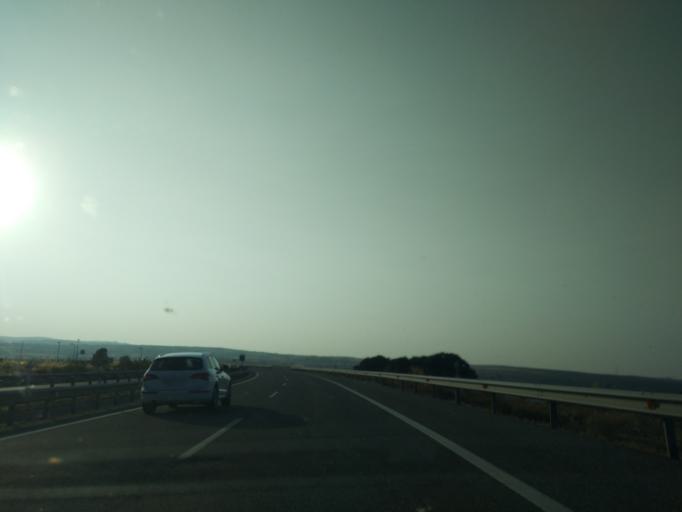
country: ES
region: Castille and Leon
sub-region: Provincia de Avila
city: Avila
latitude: 40.6765
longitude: -4.6836
